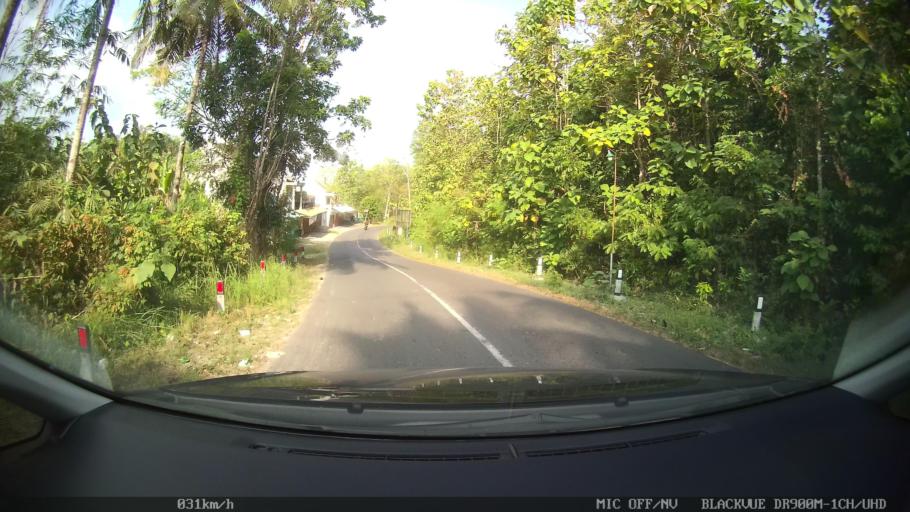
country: ID
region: Daerah Istimewa Yogyakarta
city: Bantul
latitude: -7.8585
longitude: 110.3193
